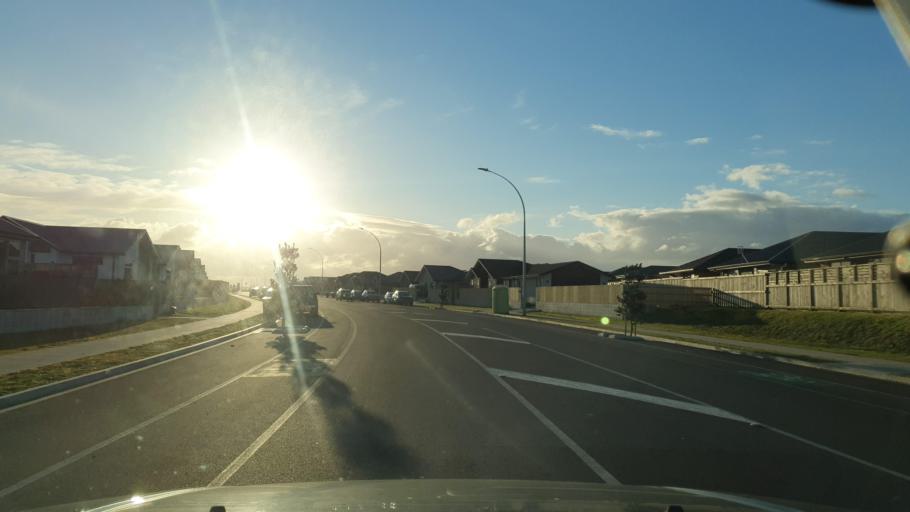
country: NZ
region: Bay of Plenty
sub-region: Western Bay of Plenty District
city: Maketu
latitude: -37.7269
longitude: 176.3360
